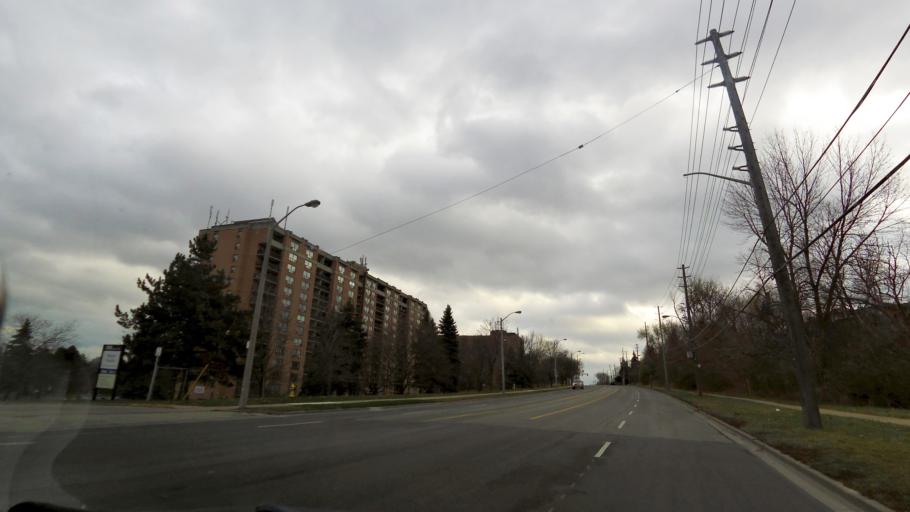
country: CA
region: Ontario
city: Etobicoke
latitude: 43.7447
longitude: -79.5685
